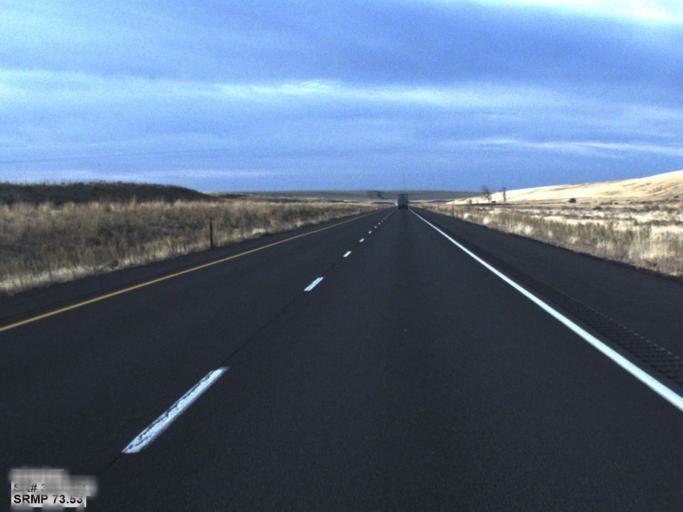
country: US
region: Washington
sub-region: Franklin County
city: Connell
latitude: 46.8557
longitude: -118.6369
